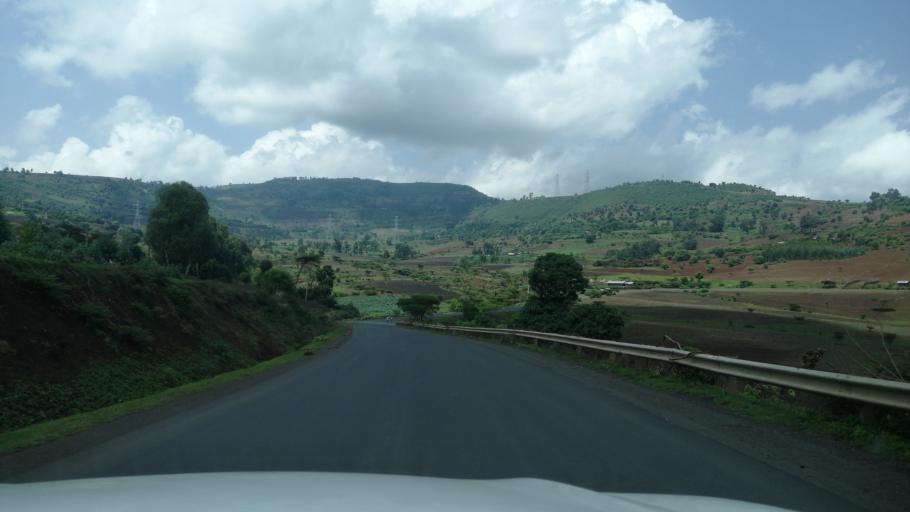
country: ET
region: Oromiya
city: Gedo
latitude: 8.9821
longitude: 37.6035
